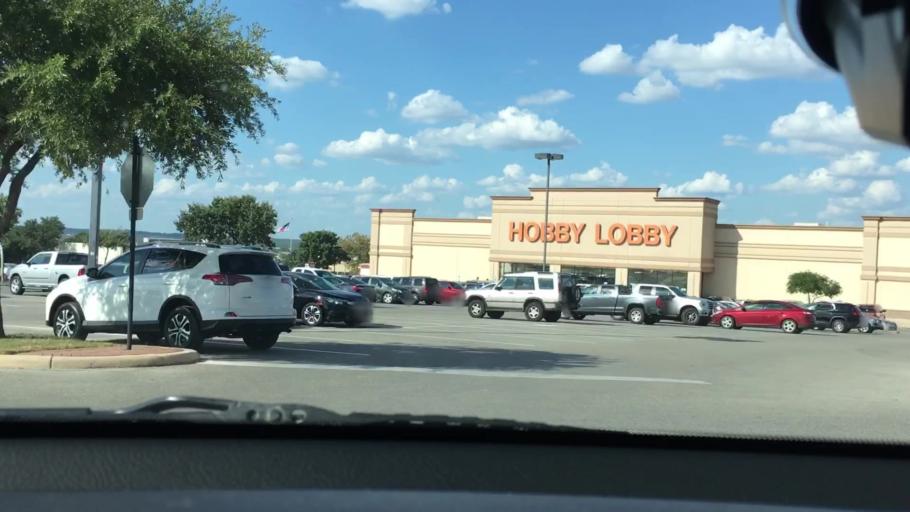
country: US
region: Texas
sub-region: Bexar County
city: Live Oak
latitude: 29.5741
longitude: -98.3227
